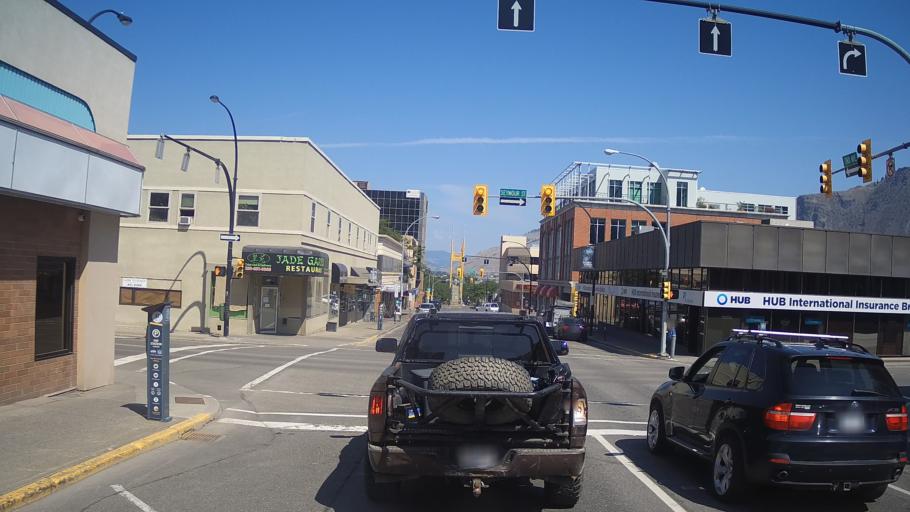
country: CA
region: British Columbia
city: Kamloops
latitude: 50.6746
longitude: -120.3345
